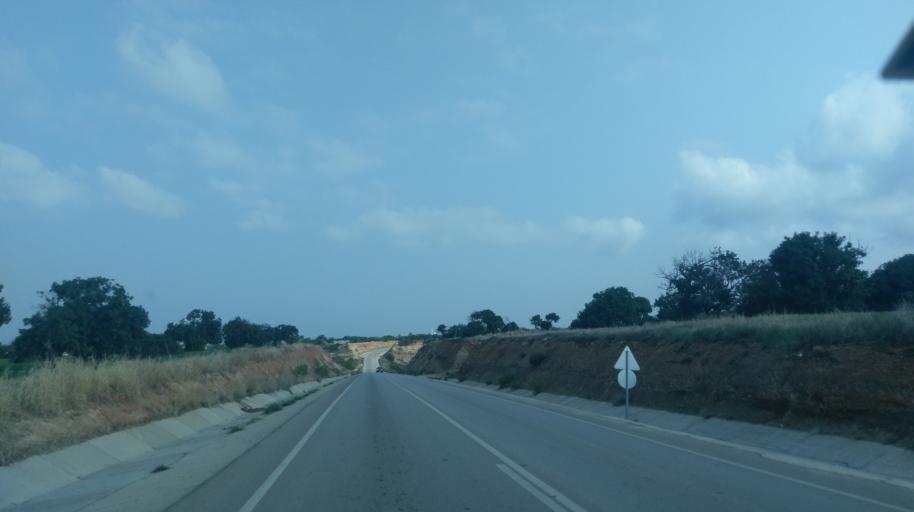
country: CY
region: Ammochostos
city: Lefkonoiko
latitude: 35.3871
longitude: 33.7276
